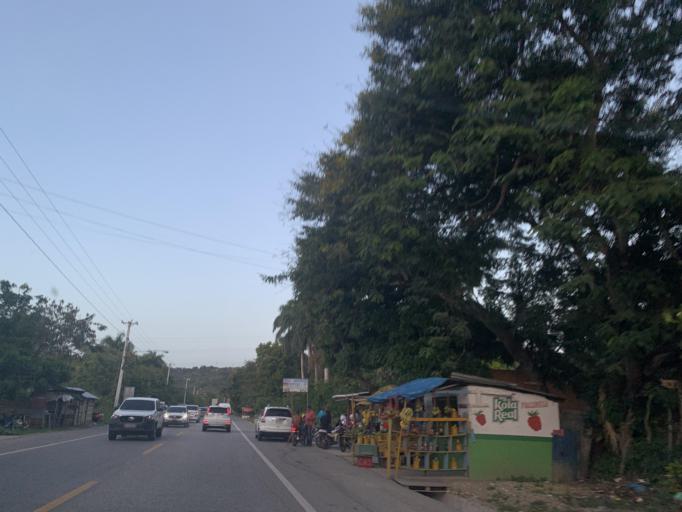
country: DO
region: Puerto Plata
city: Imbert
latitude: 19.7981
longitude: -70.7865
